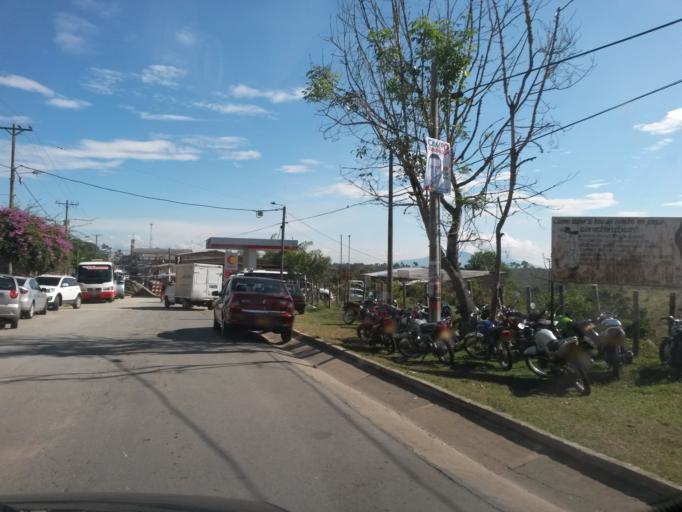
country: CO
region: Cauca
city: Morales
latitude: 2.7519
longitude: -76.6281
